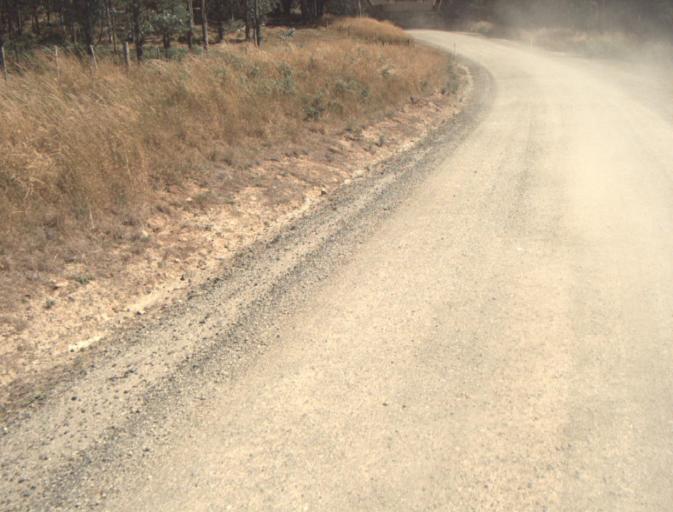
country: AU
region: Tasmania
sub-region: Dorset
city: Scottsdale
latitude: -41.3323
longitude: 147.4348
